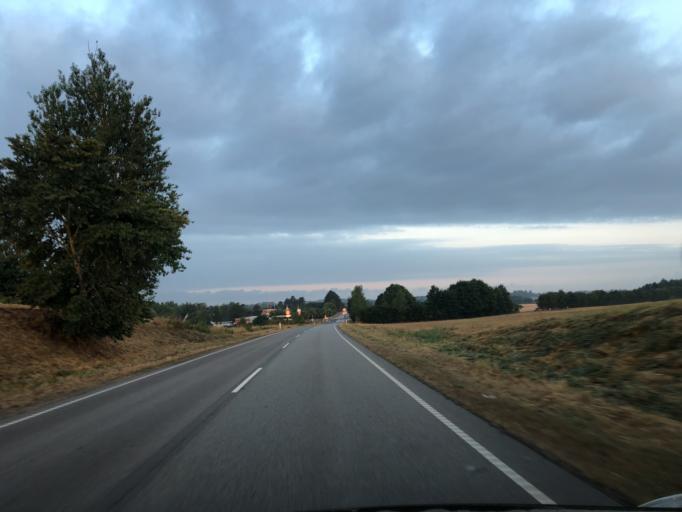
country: DK
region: Zealand
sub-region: Soro Kommune
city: Stenlille
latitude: 55.5089
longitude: 11.5562
